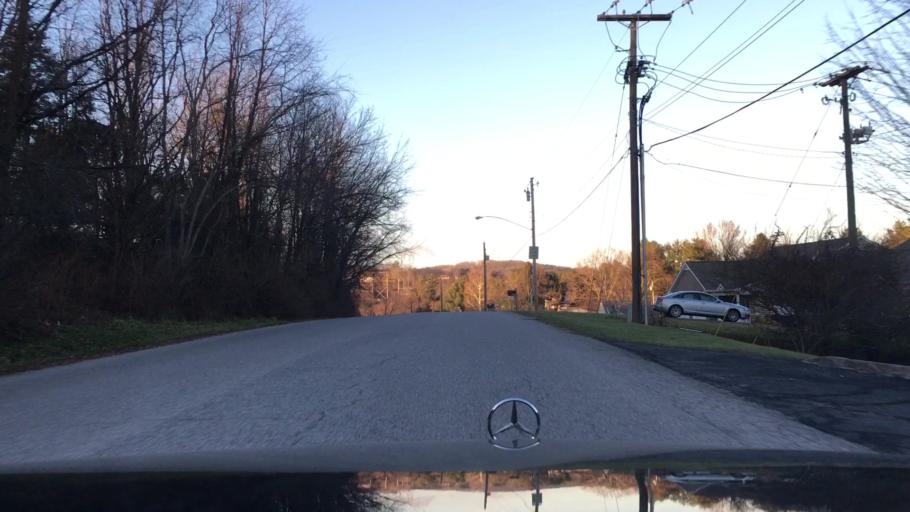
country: US
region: Virginia
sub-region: Montgomery County
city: Merrimac
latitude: 37.1646
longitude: -80.4435
